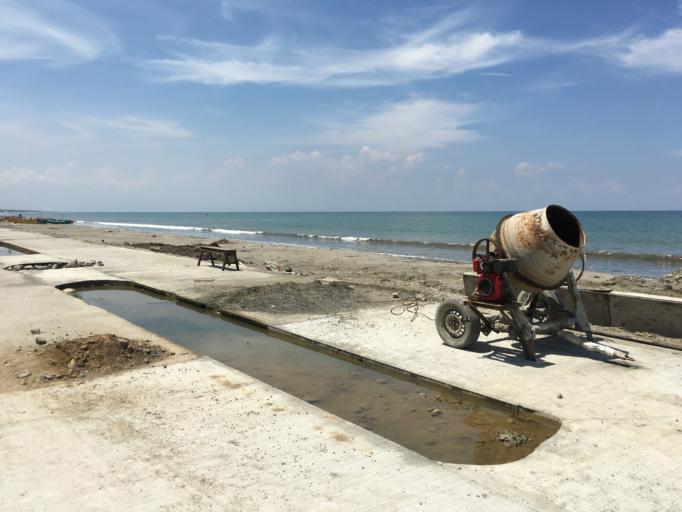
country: PH
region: Ilocos
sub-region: Province of Pangasinan
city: Mabilao
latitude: 16.1532
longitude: 120.4177
